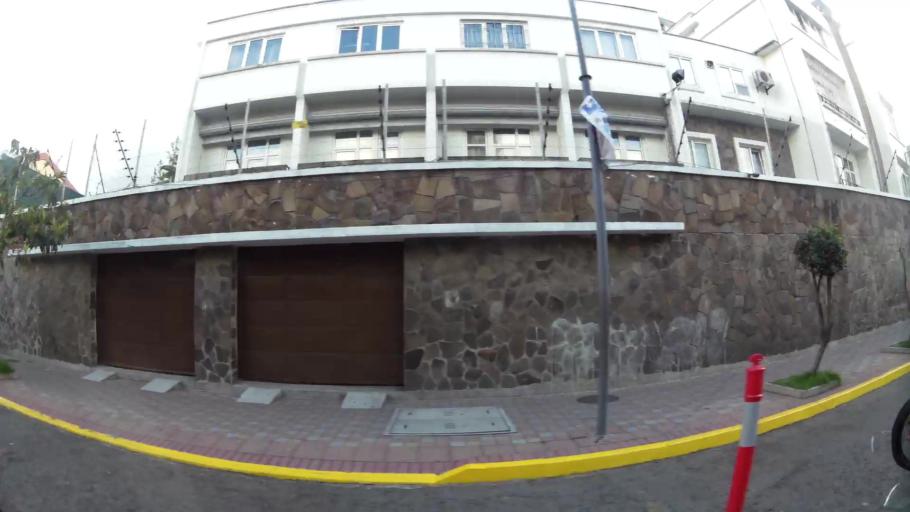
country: EC
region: Pichincha
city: Quito
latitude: -0.2062
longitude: -78.4936
